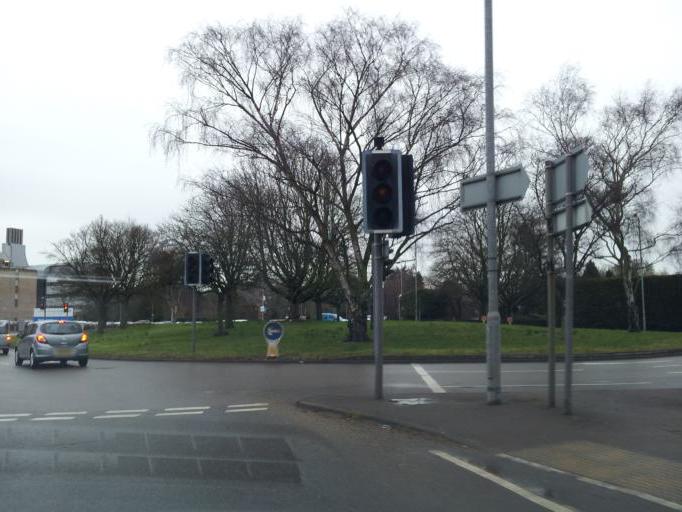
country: GB
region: England
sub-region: Cambridgeshire
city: Cambridge
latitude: 52.1762
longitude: 0.1457
